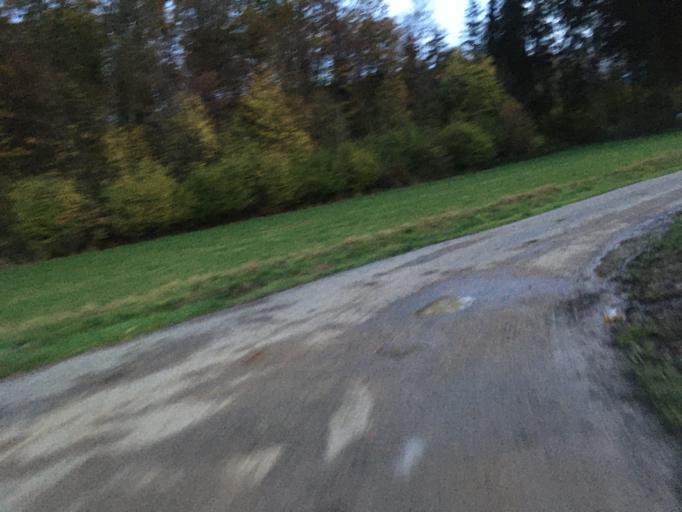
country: DE
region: Baden-Wuerttemberg
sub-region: Karlsruhe Region
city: Osterburken
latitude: 49.3808
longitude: 9.4504
